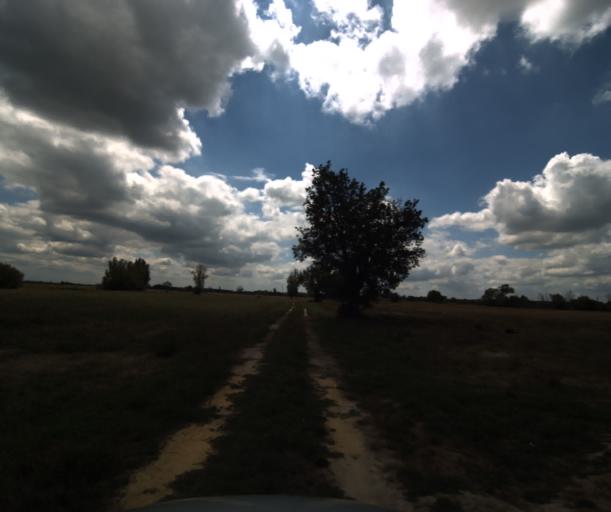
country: FR
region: Midi-Pyrenees
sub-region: Departement de la Haute-Garonne
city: Lacasse
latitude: 43.4236
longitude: 1.2551
